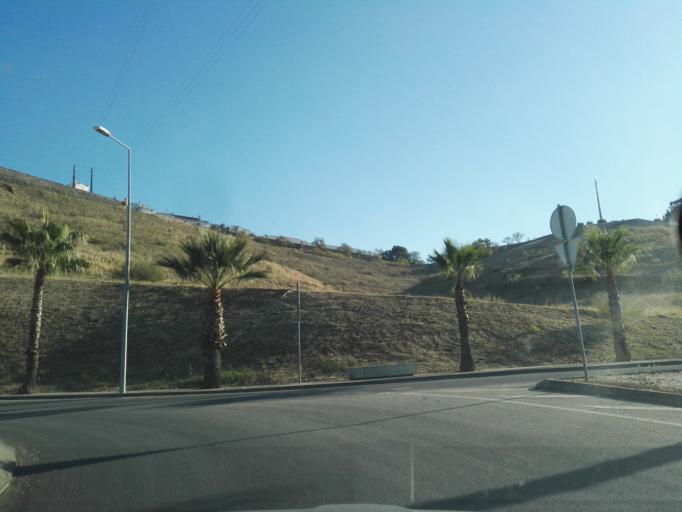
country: PT
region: Portalegre
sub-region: Elvas
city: Elvas
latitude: 38.8849
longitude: -7.1664
